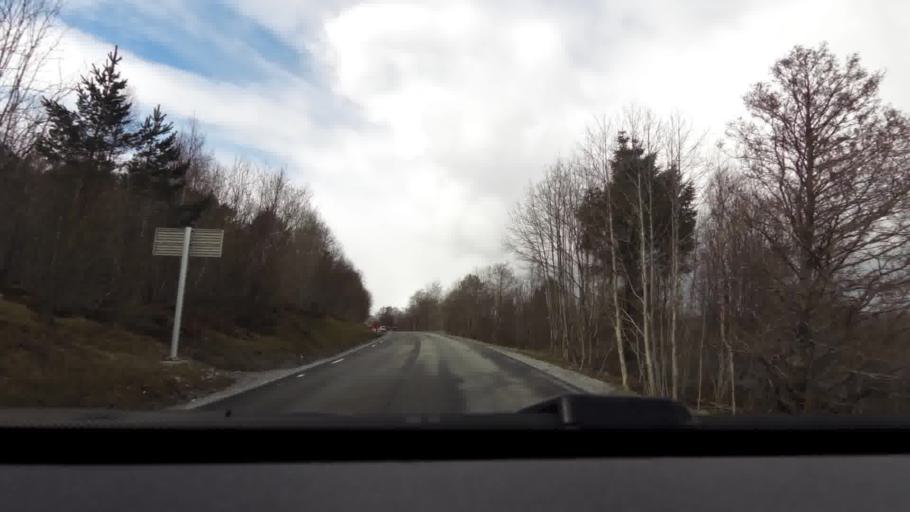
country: NO
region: More og Romsdal
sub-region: Averoy
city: Bruhagen
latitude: 63.1054
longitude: 7.6289
